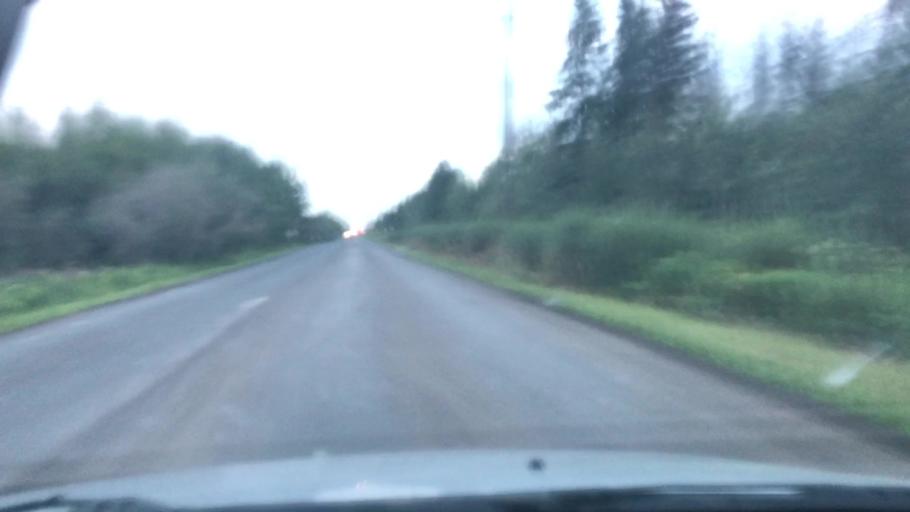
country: CA
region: Alberta
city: Devon
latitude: 53.4894
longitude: -113.6890
